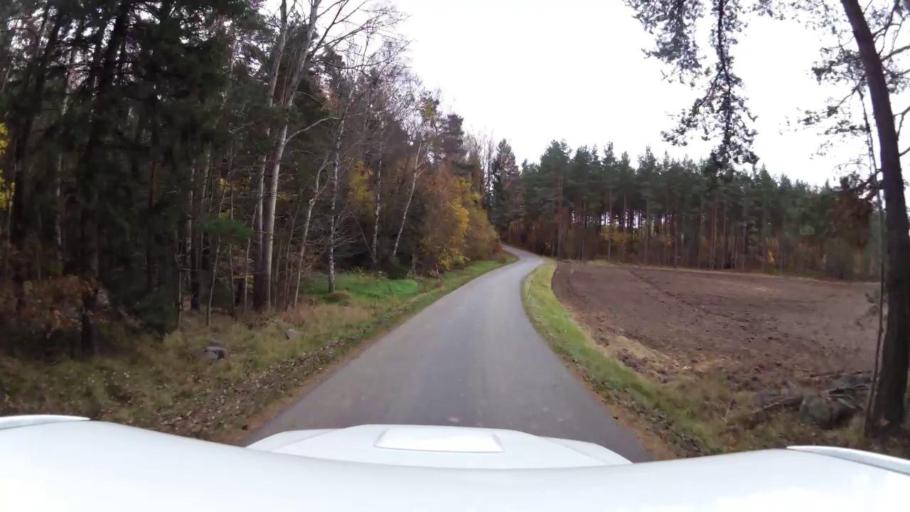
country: SE
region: OEstergoetland
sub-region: Linkopings Kommun
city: Linghem
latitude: 58.4035
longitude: 15.8449
